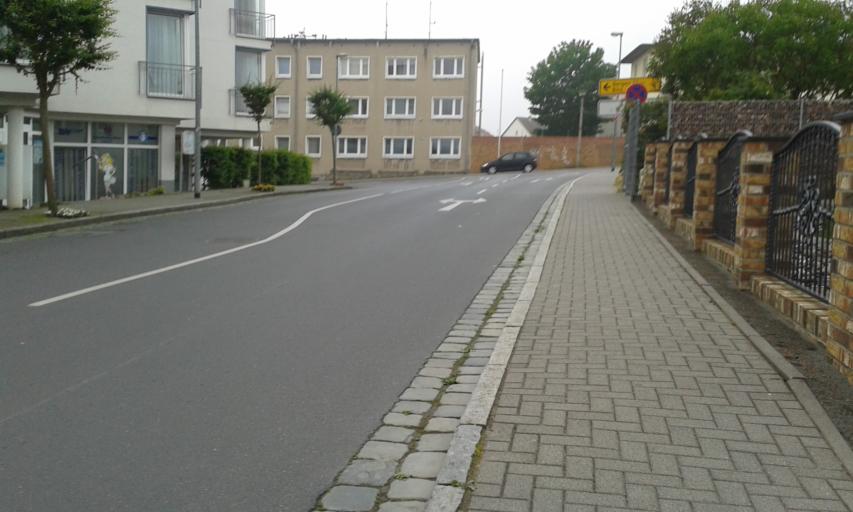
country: DE
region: Mecklenburg-Vorpommern
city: Sassnitz
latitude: 54.5157
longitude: 13.6390
